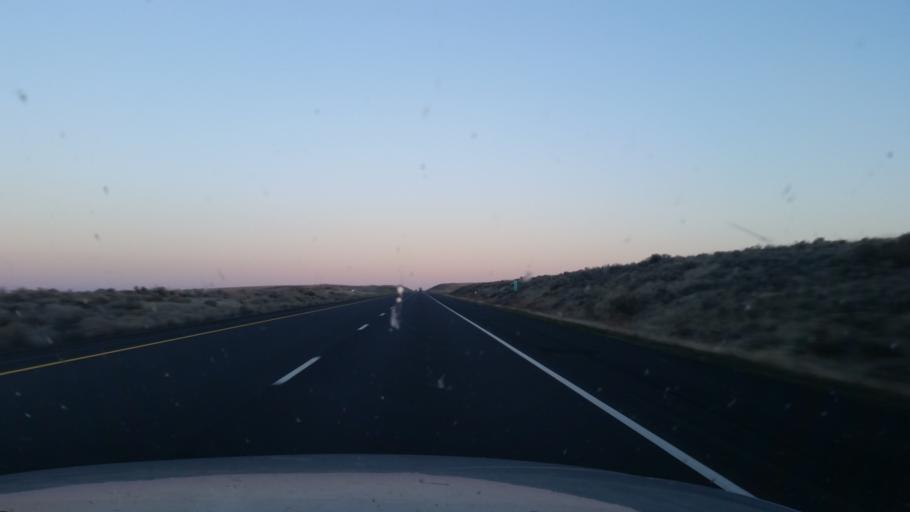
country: US
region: Washington
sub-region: Grant County
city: Warden
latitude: 47.0861
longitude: -118.7474
